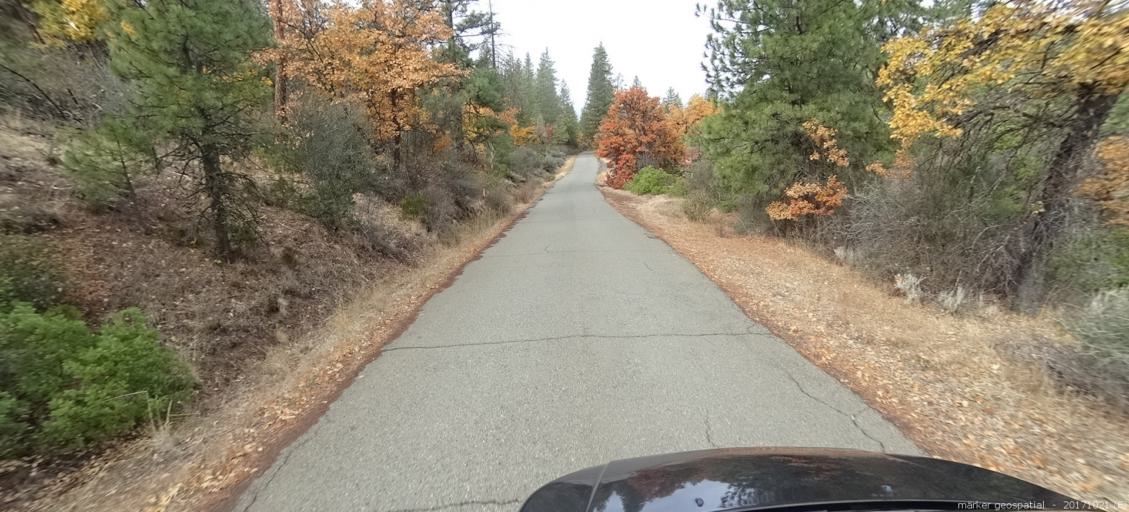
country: US
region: California
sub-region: Shasta County
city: Burney
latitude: 40.9643
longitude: -121.5598
